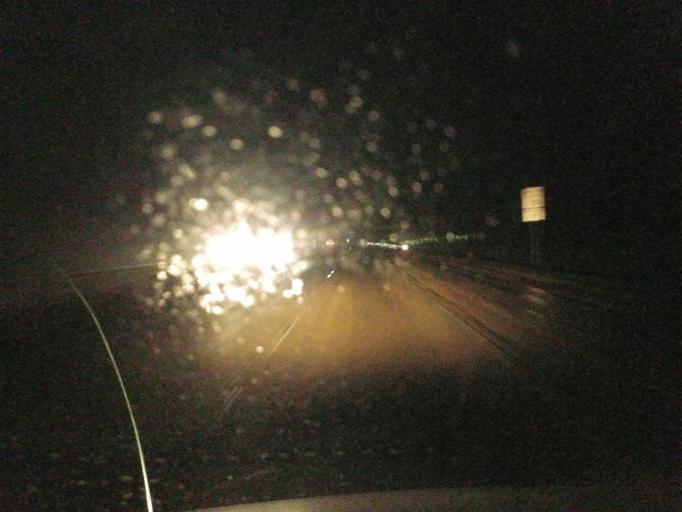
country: US
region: Illinois
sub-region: Clark County
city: Marshall
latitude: 39.4202
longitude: -87.7043
